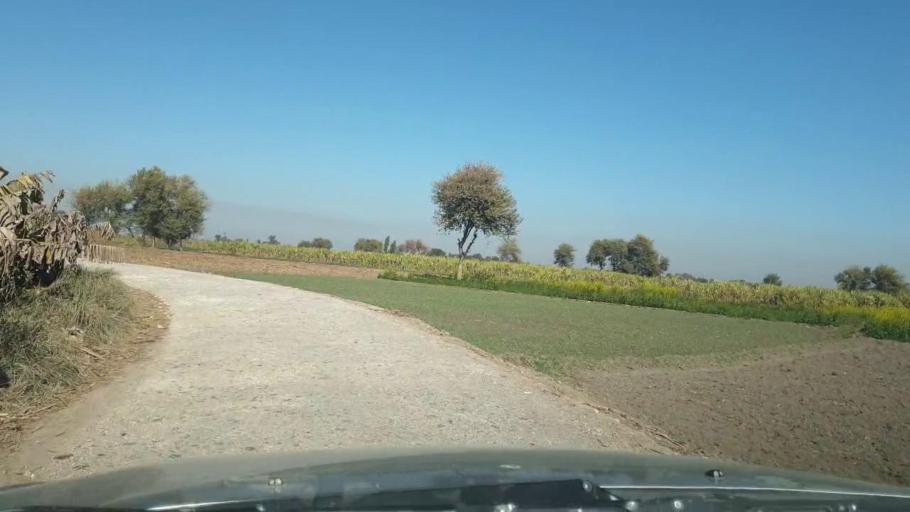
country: PK
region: Sindh
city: Ghotki
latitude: 28.0480
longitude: 69.2420
